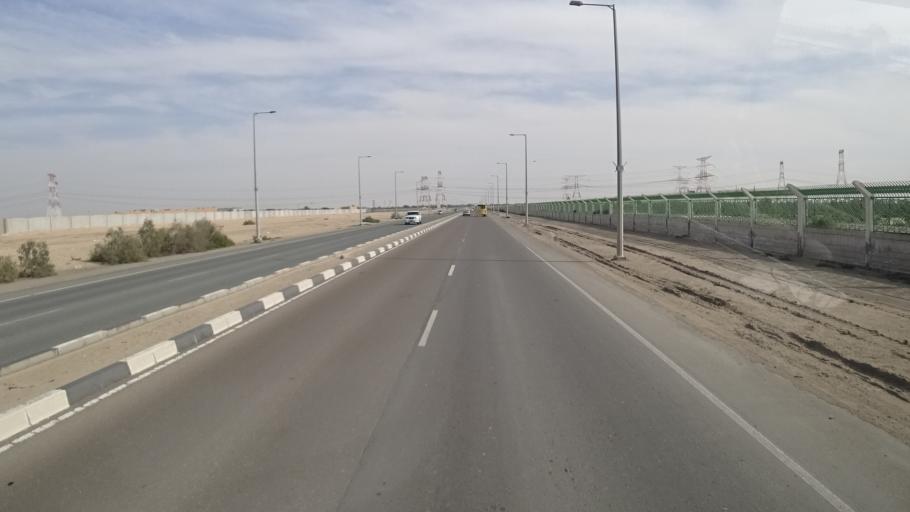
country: AE
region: Abu Dhabi
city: Abu Dhabi
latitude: 24.5296
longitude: 54.6399
